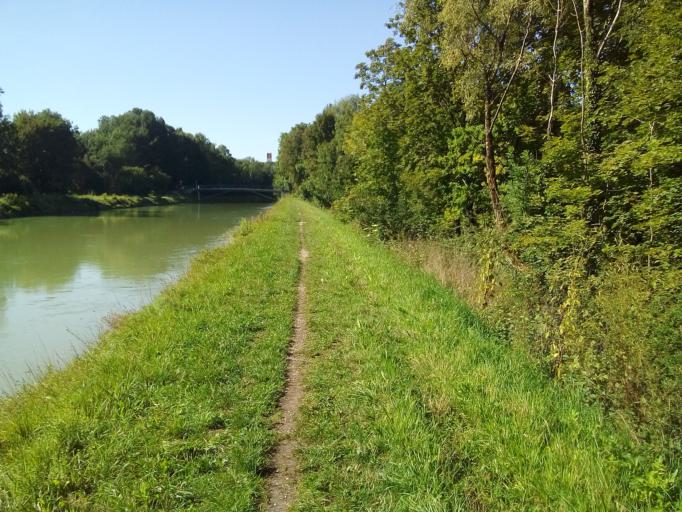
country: DE
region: Bavaria
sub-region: Upper Bavaria
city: Unterfoehring
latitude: 48.1782
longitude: 11.6267
